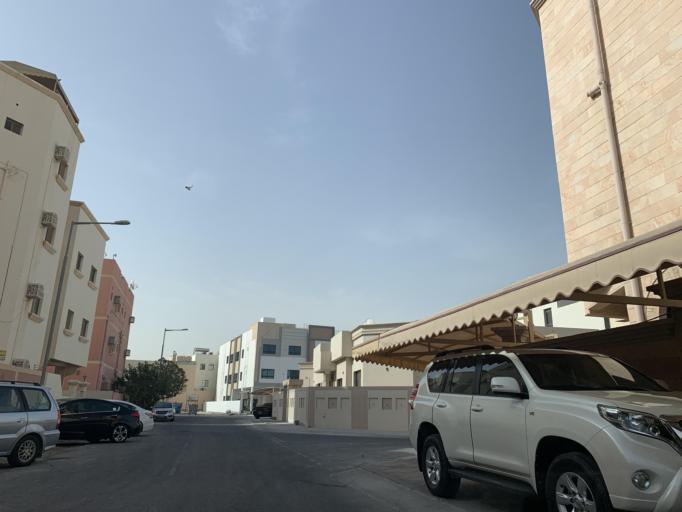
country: BH
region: Northern
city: Madinat `Isa
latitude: 26.1814
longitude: 50.5638
